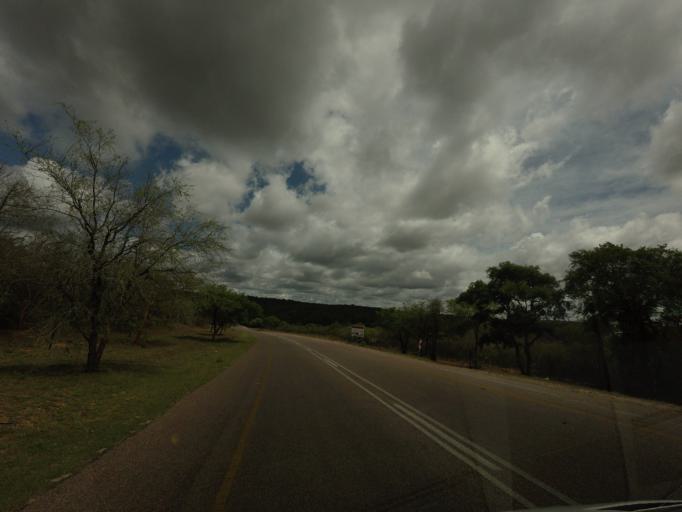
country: ZA
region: Limpopo
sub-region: Mopani District Municipality
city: Hoedspruit
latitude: -24.5449
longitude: 31.0379
